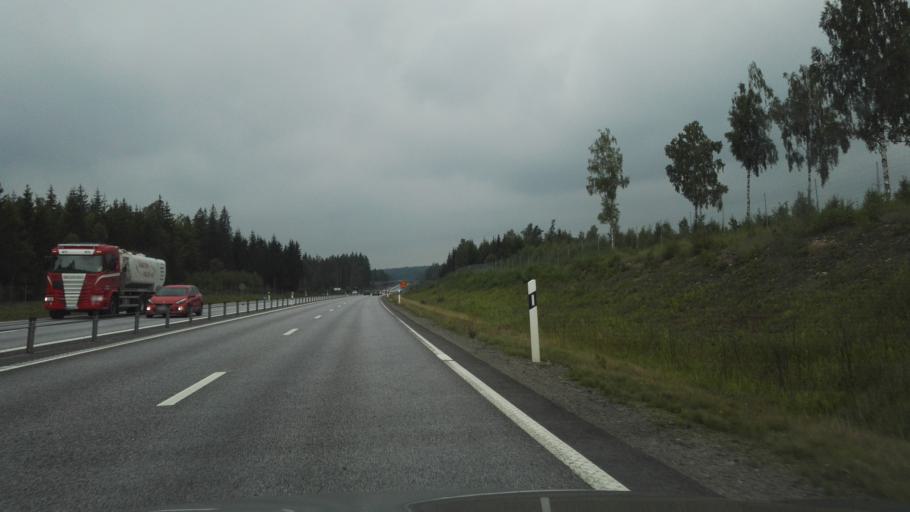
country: SE
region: Kronoberg
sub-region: Vaxjo Kommun
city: Gemla
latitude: 56.9097
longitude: 14.6412
